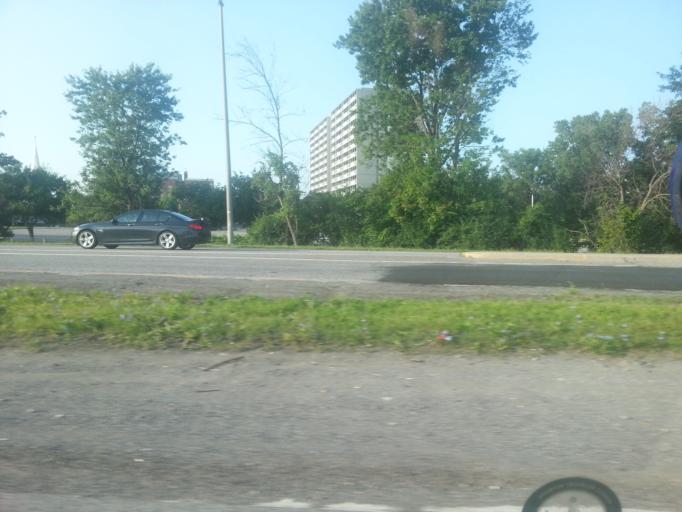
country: CA
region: Ontario
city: Ottawa
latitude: 45.4398
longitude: -75.7158
